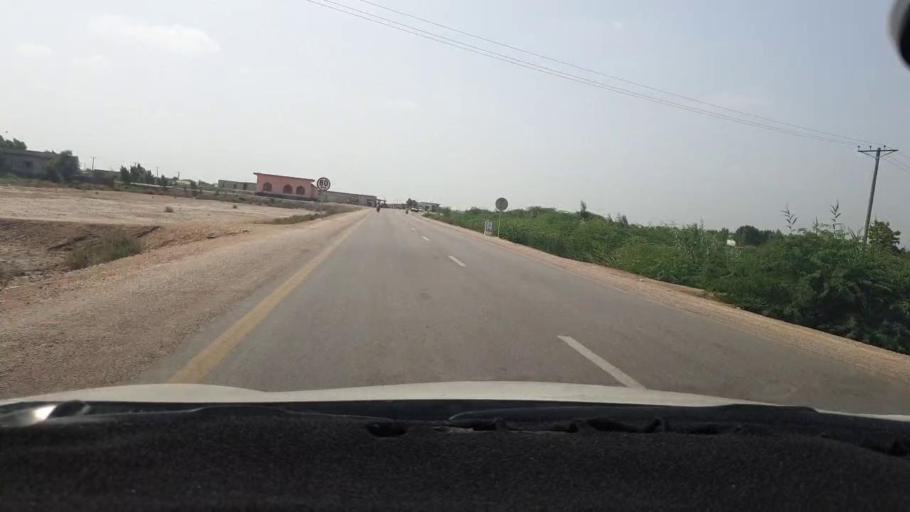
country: PK
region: Sindh
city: Mirpur Khas
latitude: 25.5987
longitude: 69.0836
